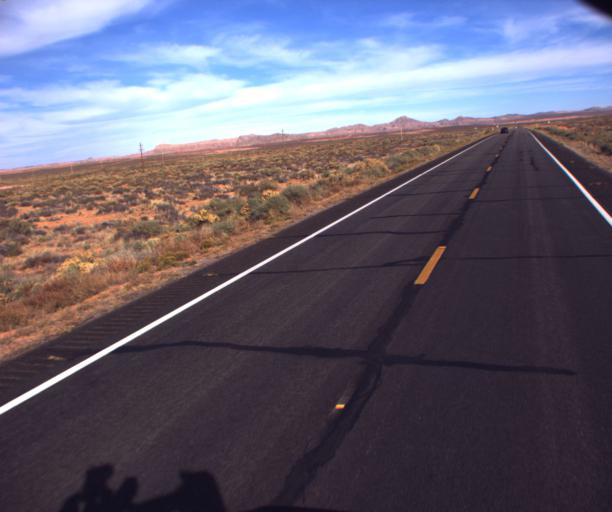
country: US
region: Arizona
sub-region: Apache County
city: Many Farms
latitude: 36.9408
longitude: -109.6643
